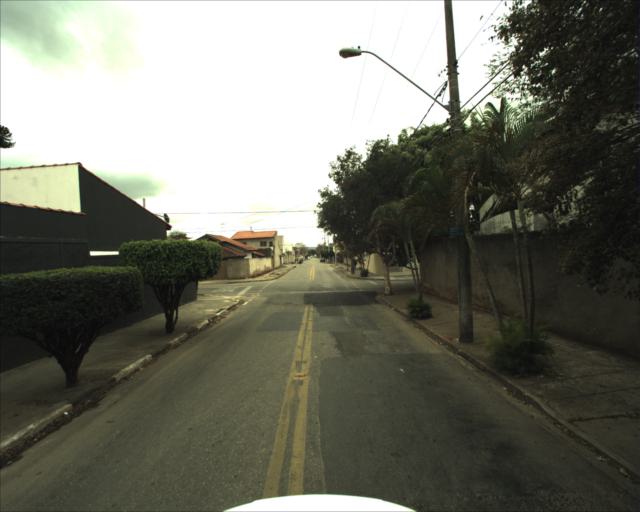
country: BR
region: Sao Paulo
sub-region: Sorocaba
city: Sorocaba
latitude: -23.5087
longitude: -47.5151
